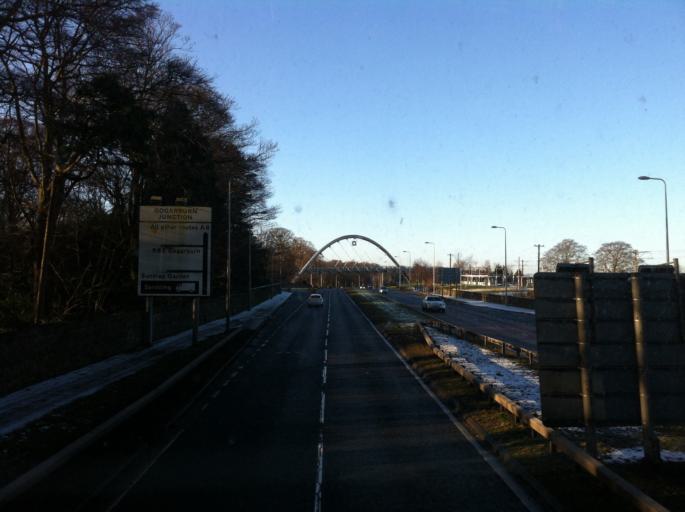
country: GB
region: Scotland
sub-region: Edinburgh
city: Currie
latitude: 55.9383
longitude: -3.3291
